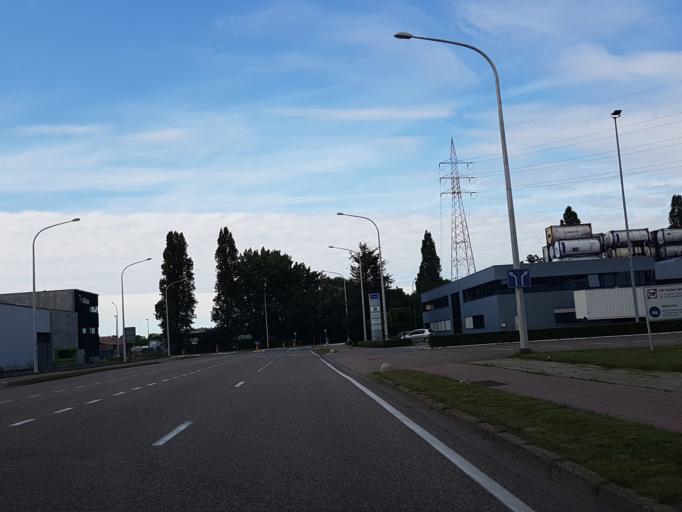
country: BE
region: Flanders
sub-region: Provincie Antwerpen
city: Antwerpen
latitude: 51.2721
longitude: 4.4008
